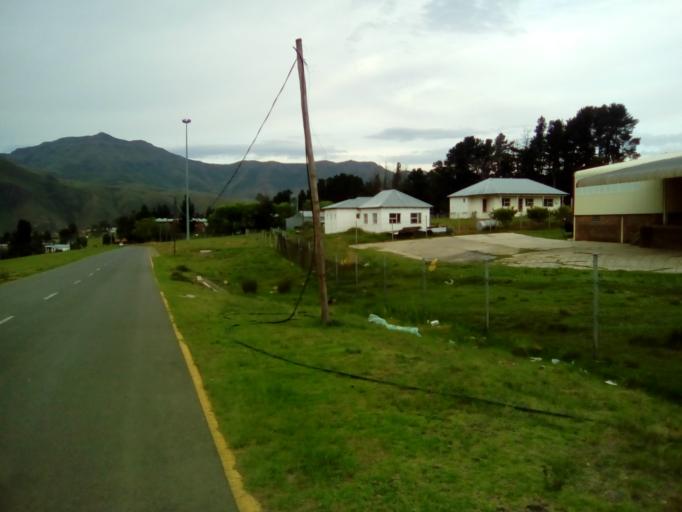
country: LS
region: Qacha's Nek
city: Qacha's Nek
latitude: -30.1143
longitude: 28.6803
